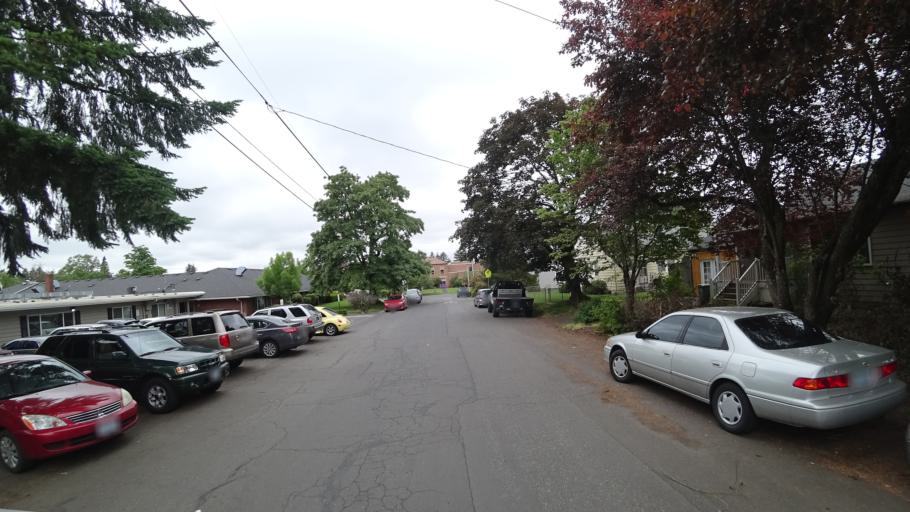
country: US
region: Oregon
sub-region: Multnomah County
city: Portland
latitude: 45.5547
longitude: -122.6075
